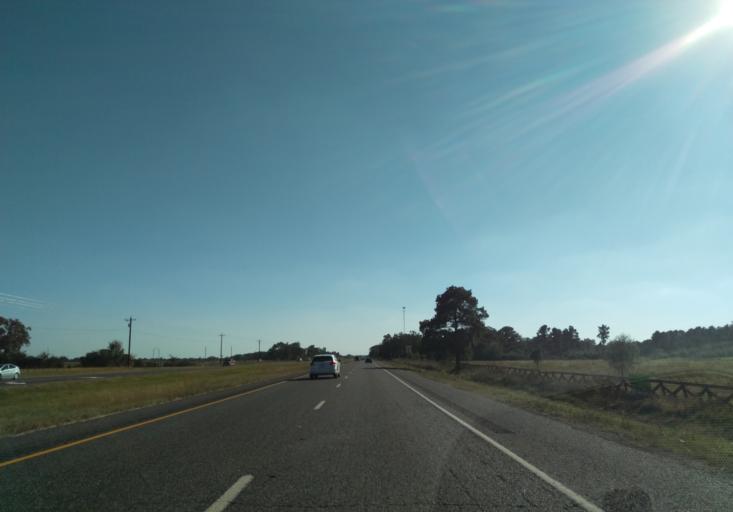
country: US
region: Texas
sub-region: Waller County
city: Hempstead
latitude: 30.1395
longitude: -96.0717
